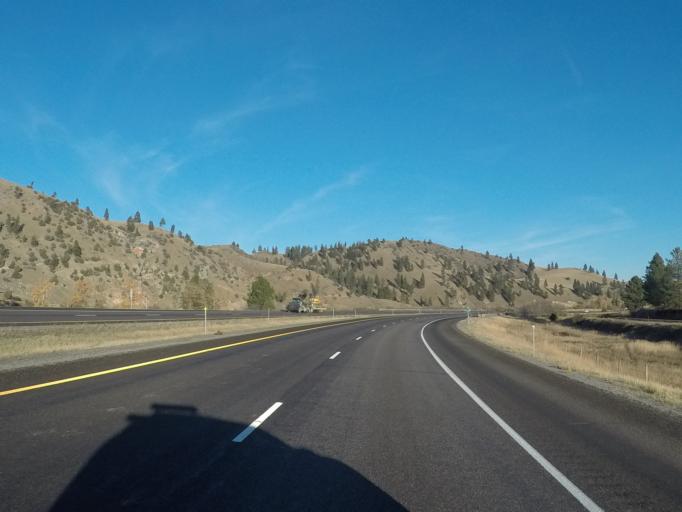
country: US
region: Montana
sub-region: Missoula County
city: Clinton
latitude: 46.7041
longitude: -113.3785
